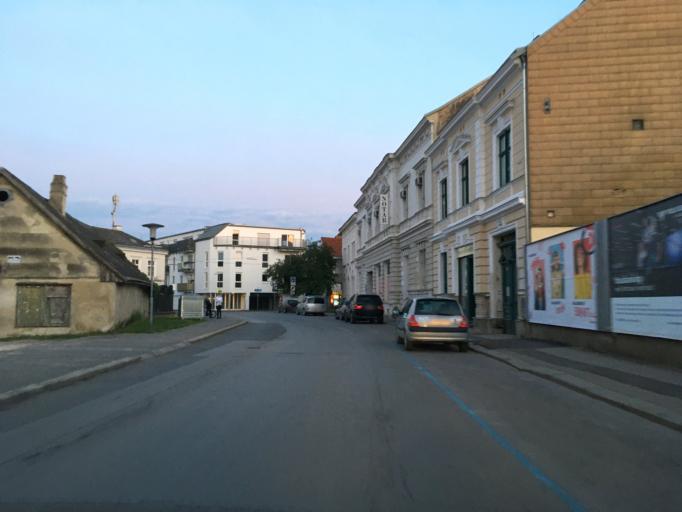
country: AT
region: Lower Austria
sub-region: Politischer Bezirk Korneuburg
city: Stockerau
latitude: 48.3844
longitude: 16.2104
